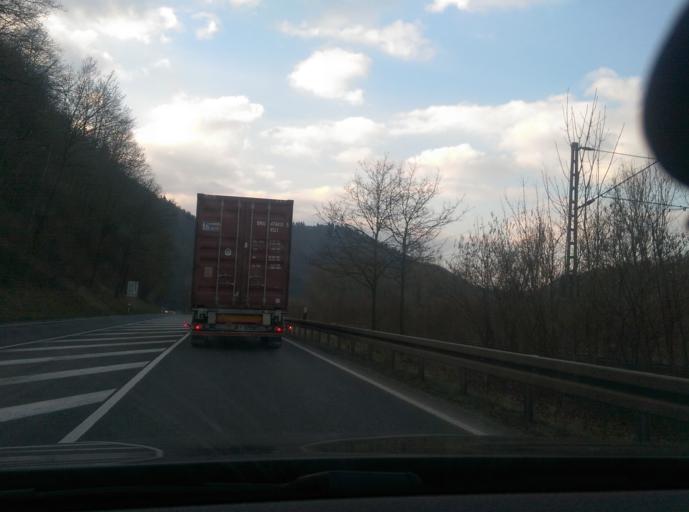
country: DE
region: Hesse
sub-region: Regierungsbezirk Kassel
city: Bad Sooden-Allendorf
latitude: 51.2343
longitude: 9.9876
